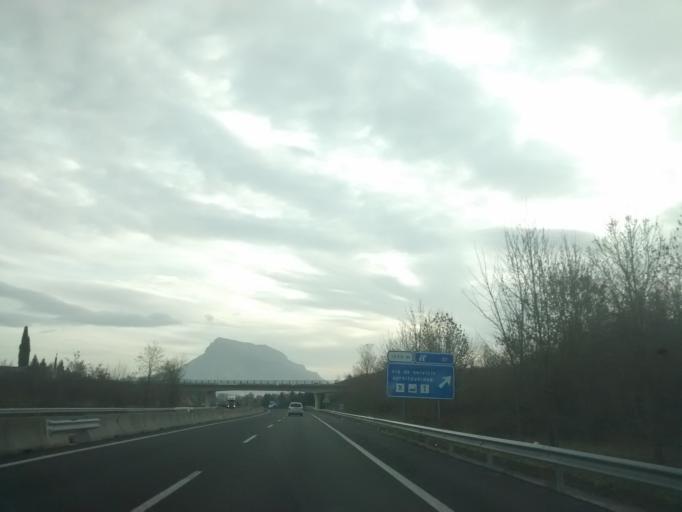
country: ES
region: Navarre
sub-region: Provincia de Navarra
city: Bakaiku
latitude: 42.8931
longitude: -2.0985
